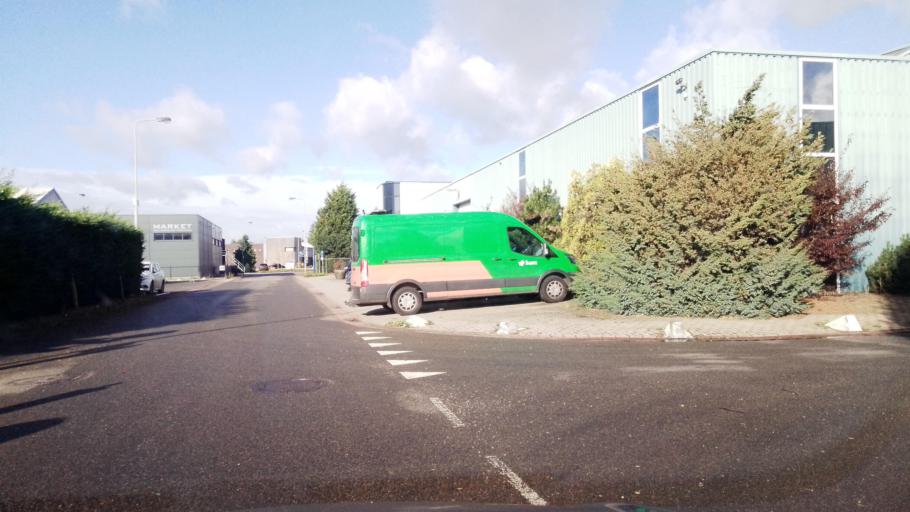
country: NL
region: Limburg
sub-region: Gemeente Venlo
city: Arcen
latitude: 51.4472
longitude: 6.1765
